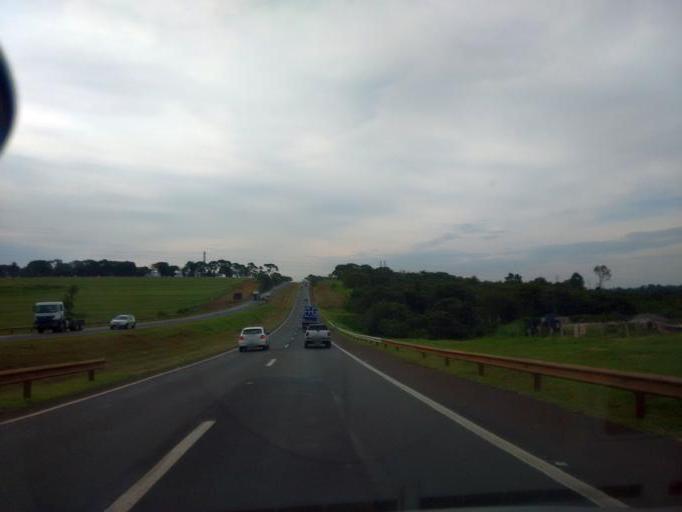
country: BR
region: Sao Paulo
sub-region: Araraquara
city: Araraquara
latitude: -21.7944
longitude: -48.2112
